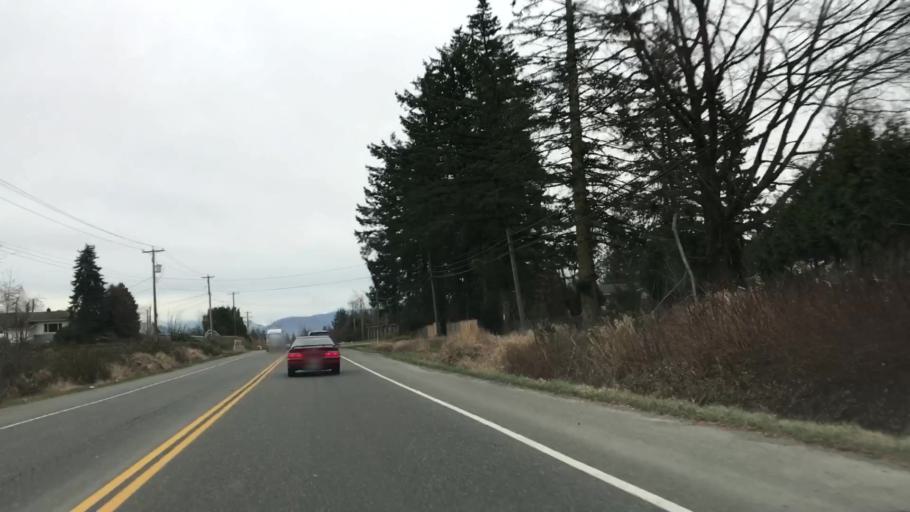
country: CA
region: British Columbia
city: Aldergrove
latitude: 49.0574
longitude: -122.4110
